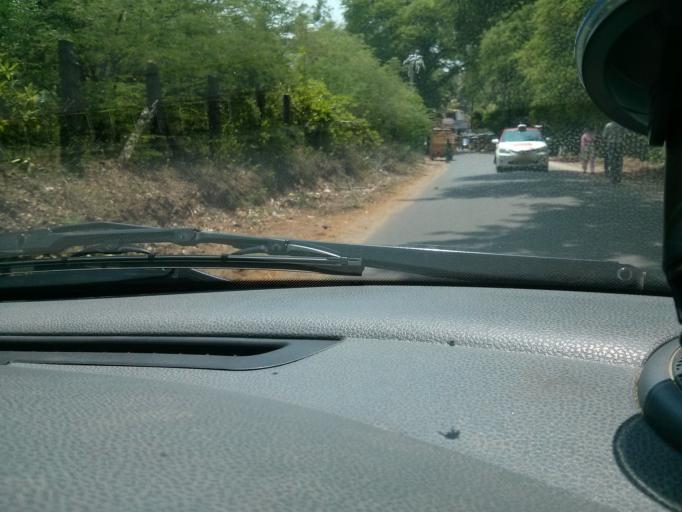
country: IN
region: Tamil Nadu
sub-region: Coimbatore
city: Periyanayakkanpalaiyam
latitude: 11.1031
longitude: 76.9370
